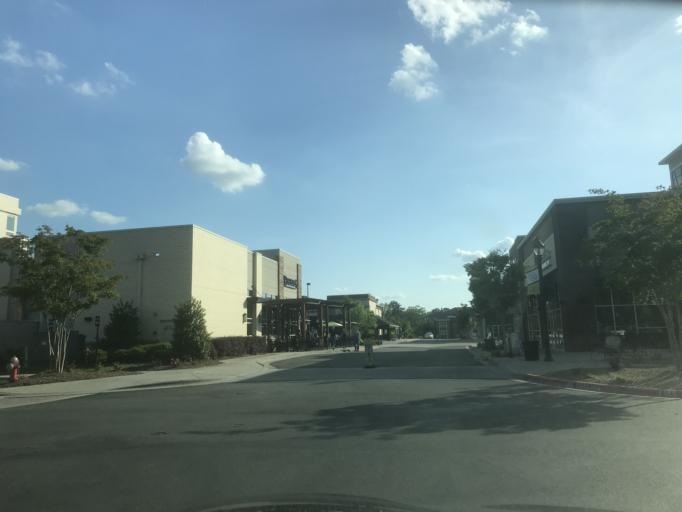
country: US
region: North Carolina
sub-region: Wake County
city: Morrisville
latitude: 35.8082
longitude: -78.8185
